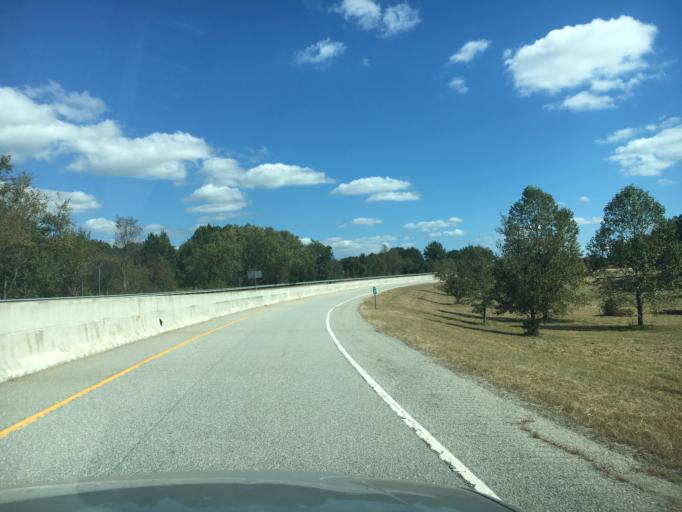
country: US
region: South Carolina
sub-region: Spartanburg County
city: Valley Falls
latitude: 35.0126
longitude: -81.9128
